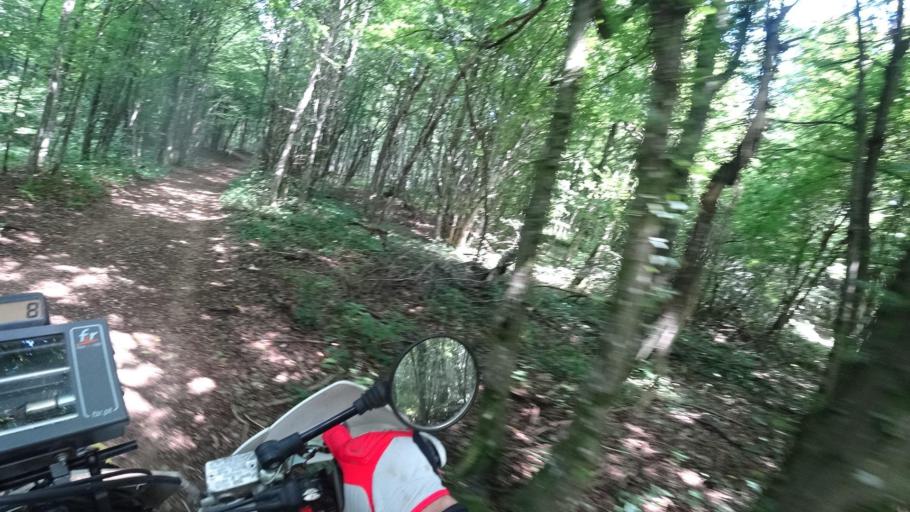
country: HR
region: Karlovacka
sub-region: Grad Ogulin
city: Ogulin
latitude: 45.2505
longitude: 15.1886
